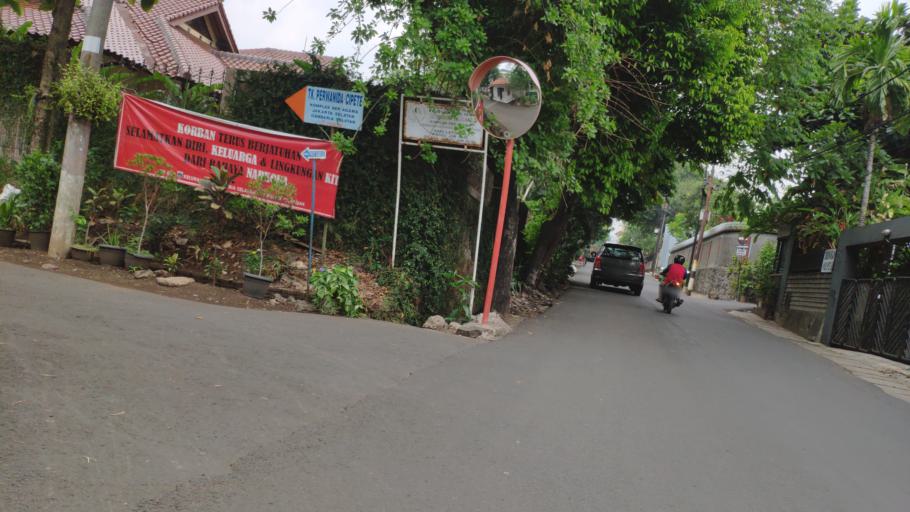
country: ID
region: Jakarta Raya
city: Jakarta
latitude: -6.2673
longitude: 106.7951
